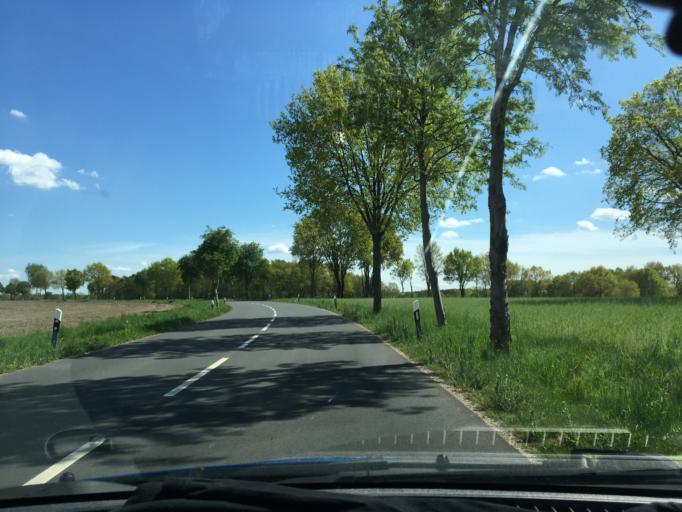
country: DE
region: Lower Saxony
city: Himbergen
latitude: 53.0816
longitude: 10.7482
